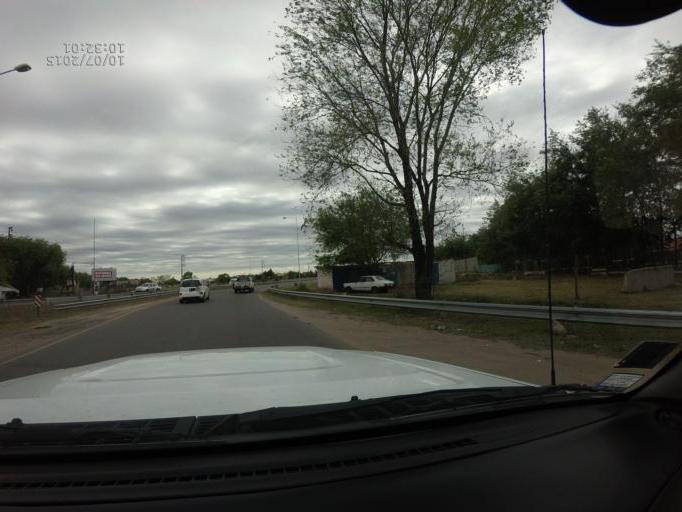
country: AR
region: Cordoba
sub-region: Departamento de Capital
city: Cordoba
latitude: -31.3542
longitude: -64.2339
